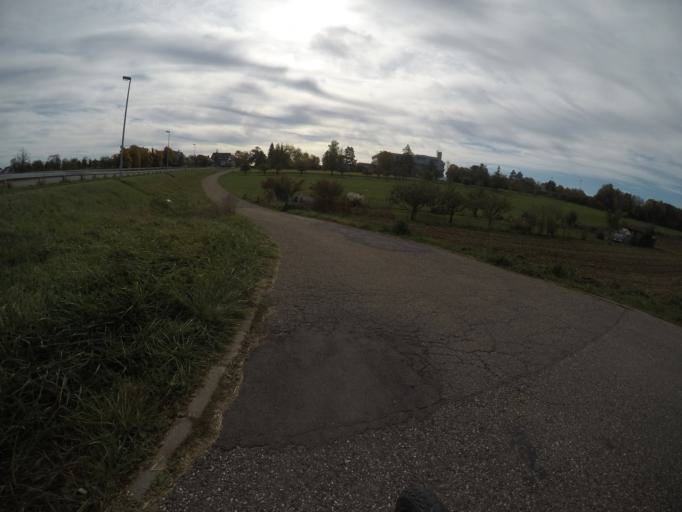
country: DE
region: Baden-Wuerttemberg
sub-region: Regierungsbezirk Stuttgart
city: Herrenberg
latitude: 48.6172
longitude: 8.8405
